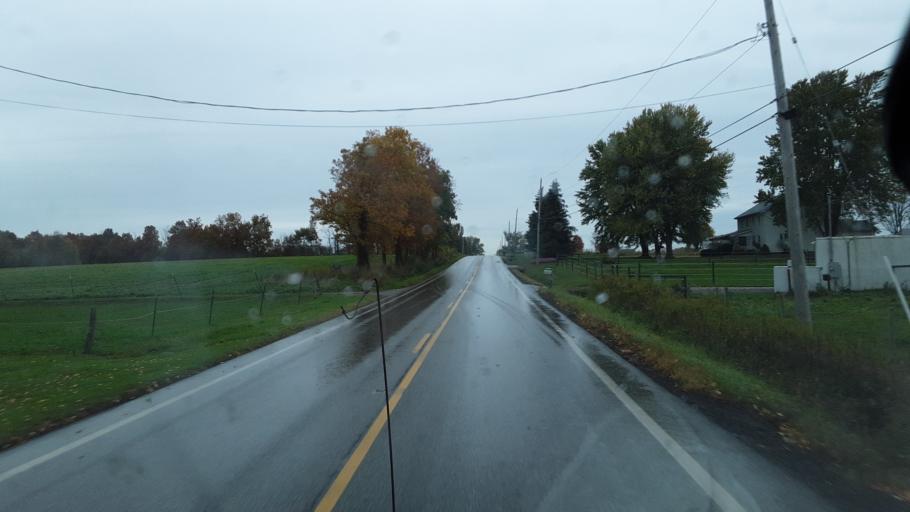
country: US
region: Ohio
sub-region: Geauga County
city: Middlefield
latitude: 41.3943
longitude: -81.0874
